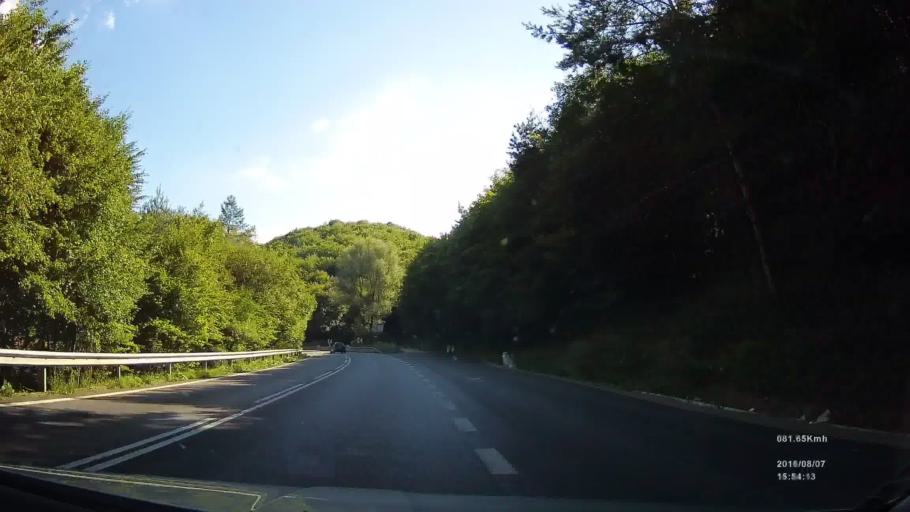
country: SK
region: Presovsky
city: Giraltovce
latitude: 49.0902
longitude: 21.4442
